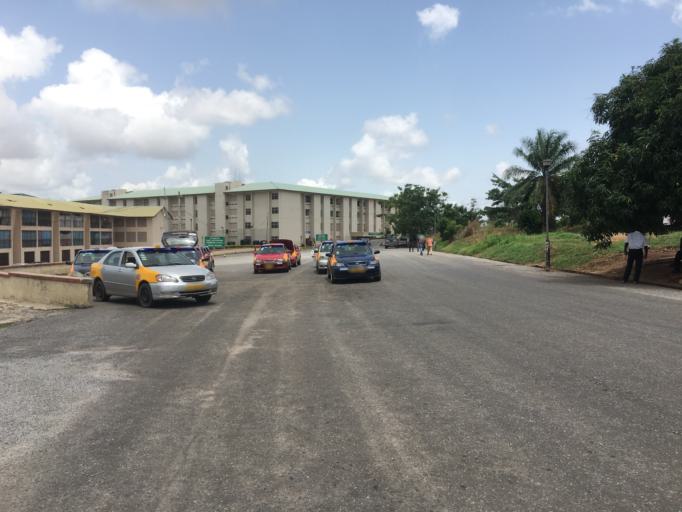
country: GH
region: Ashanti
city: Kumasi
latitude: 6.6708
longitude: -1.5738
